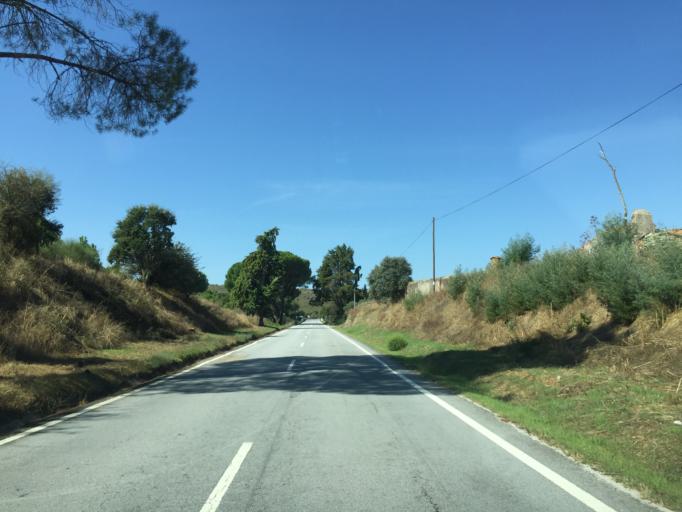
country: PT
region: Portalegre
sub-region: Portalegre
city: Alagoa
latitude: 39.4343
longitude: -7.5336
